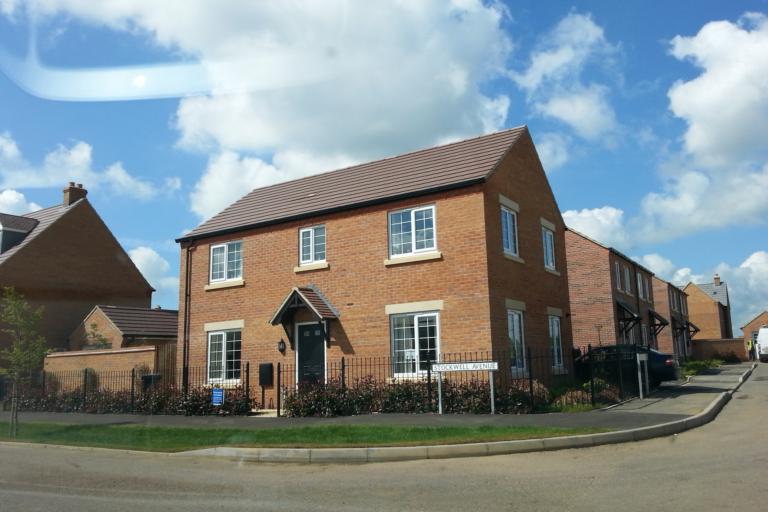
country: GB
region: England
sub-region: District of Rutland
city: Tinwell
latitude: 52.6535
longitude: -0.5057
